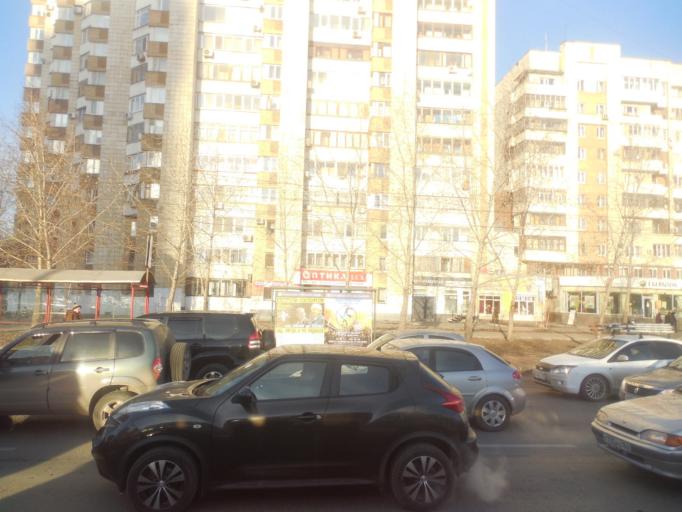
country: RU
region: Samara
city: Samara
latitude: 53.2037
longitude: 50.1269
